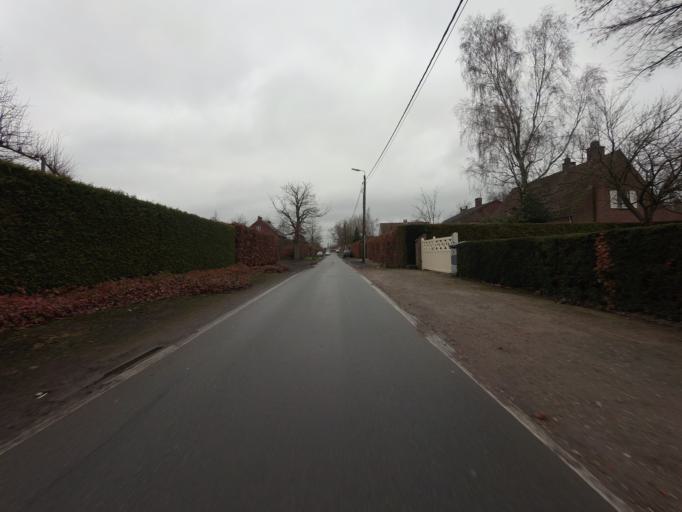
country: BE
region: Flanders
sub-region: Provincie Antwerpen
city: Sint-Katelijne-Waver
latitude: 51.0496
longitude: 4.5423
